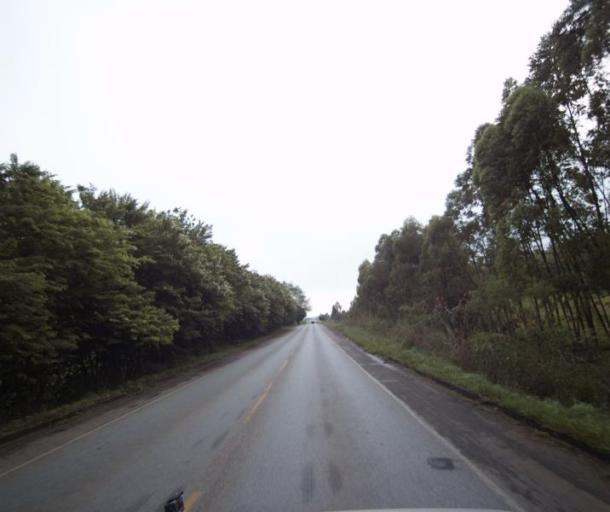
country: BR
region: Goias
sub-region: Pirenopolis
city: Pirenopolis
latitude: -15.8030
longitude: -48.7796
